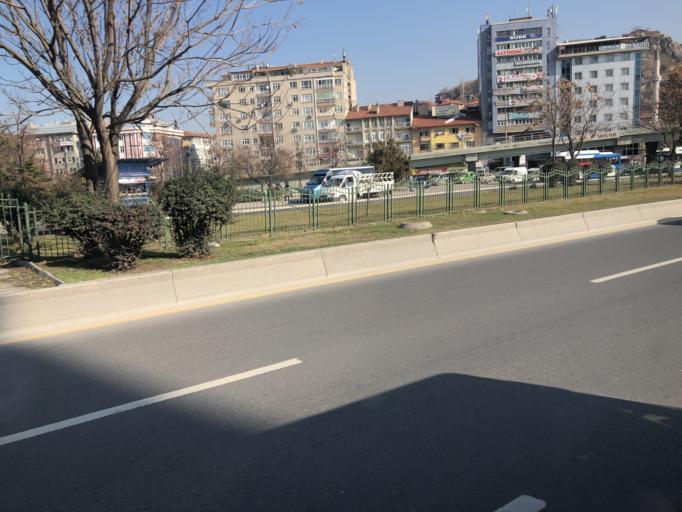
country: TR
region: Ankara
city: Ankara
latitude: 39.9520
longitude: 32.8574
